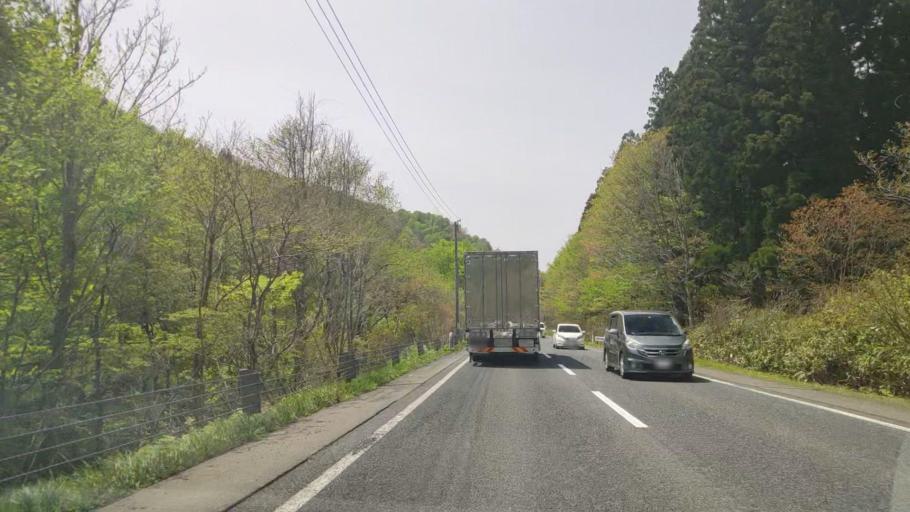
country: JP
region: Aomori
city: Aomori Shi
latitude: 40.7759
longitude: 141.0155
